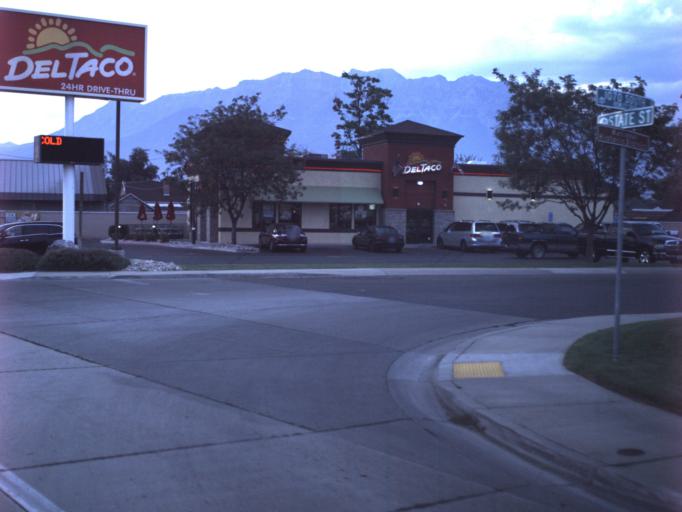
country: US
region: Utah
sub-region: Utah County
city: Orem
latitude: 40.2773
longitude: -111.6861
